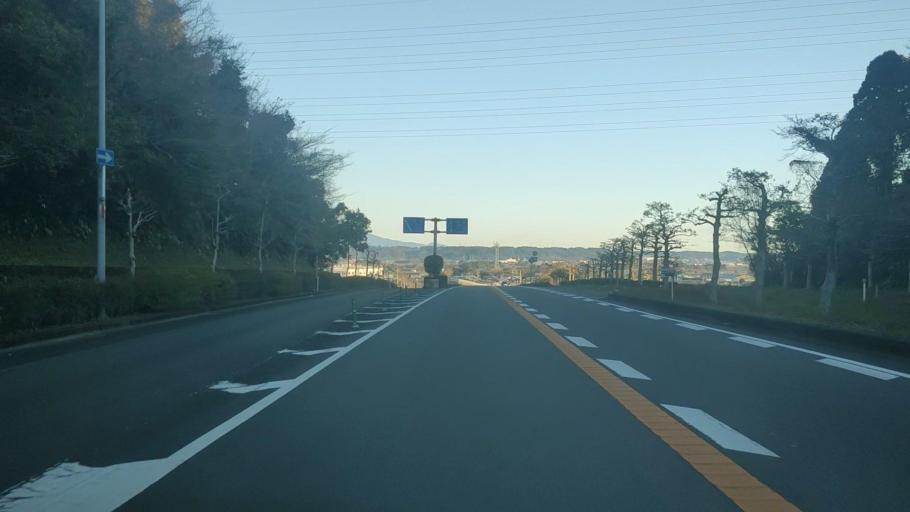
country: JP
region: Miyazaki
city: Tsuma
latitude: 32.0323
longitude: 131.4649
